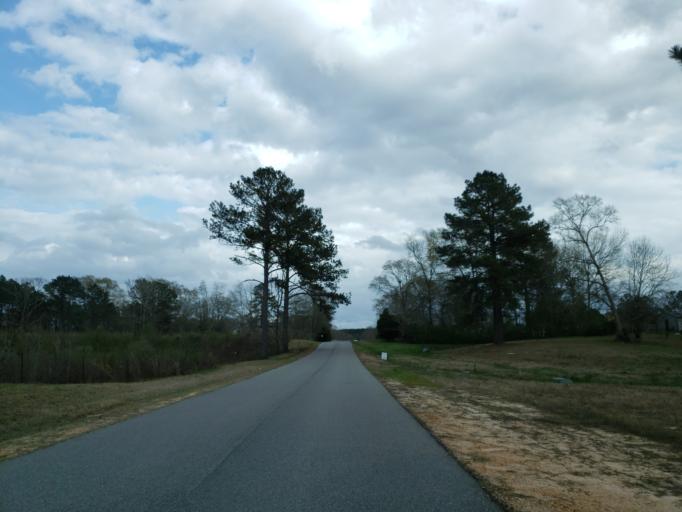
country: US
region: Mississippi
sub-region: Jones County
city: Ellisville
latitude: 31.5624
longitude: -89.2457
